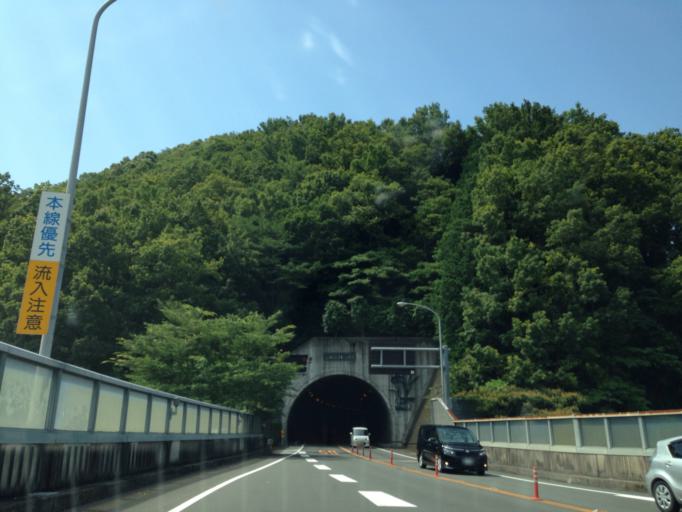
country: JP
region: Shizuoka
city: Mishima
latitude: 35.0272
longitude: 138.9246
